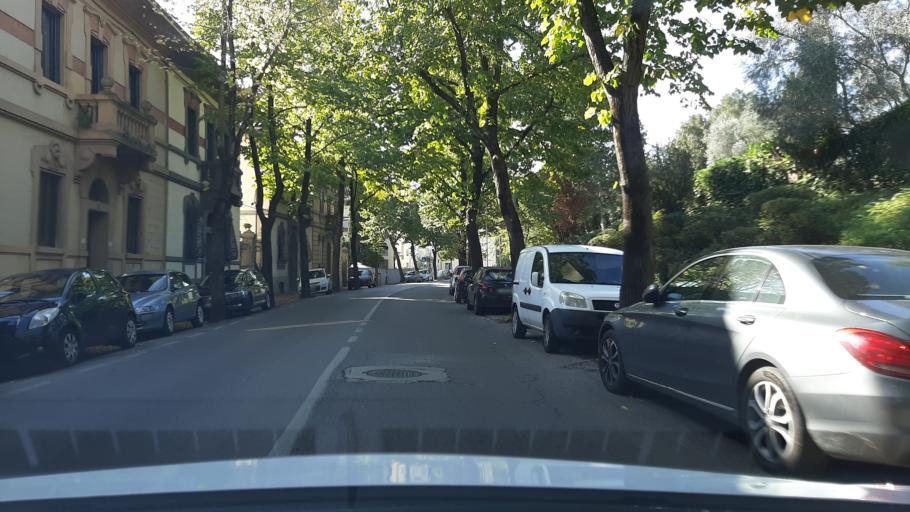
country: IT
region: Tuscany
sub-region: Province of Florence
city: Fiesole
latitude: 43.7851
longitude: 11.2925
